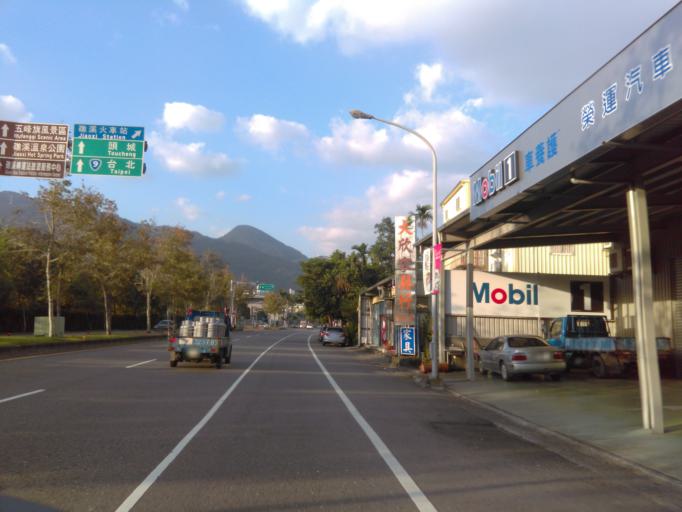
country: TW
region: Taiwan
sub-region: Yilan
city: Yilan
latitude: 24.8143
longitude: 121.7677
